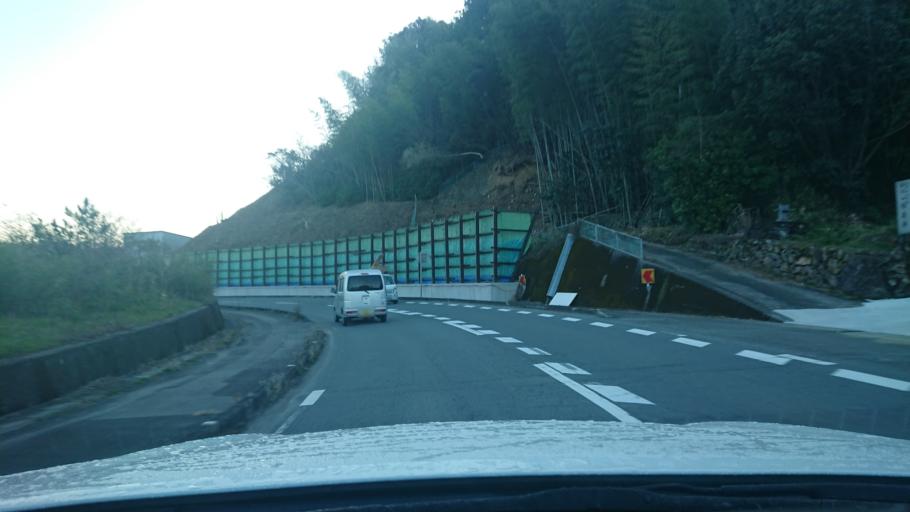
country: JP
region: Tokushima
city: Komatsushimacho
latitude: 33.9489
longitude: 134.5583
